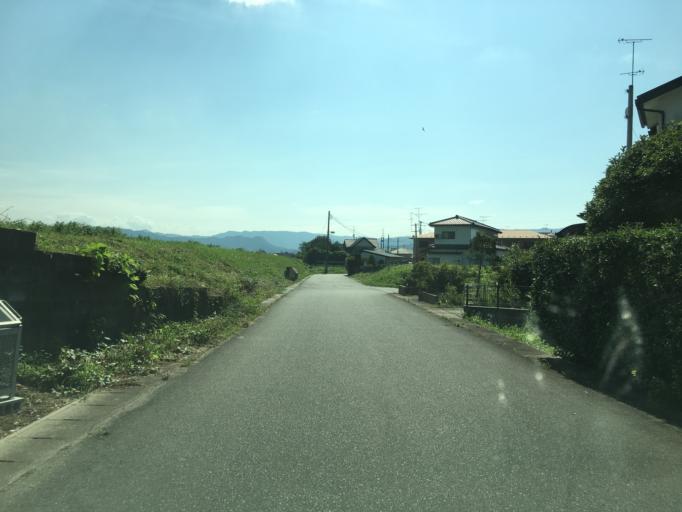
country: JP
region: Miyagi
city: Marumori
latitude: 37.8017
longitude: 140.9343
